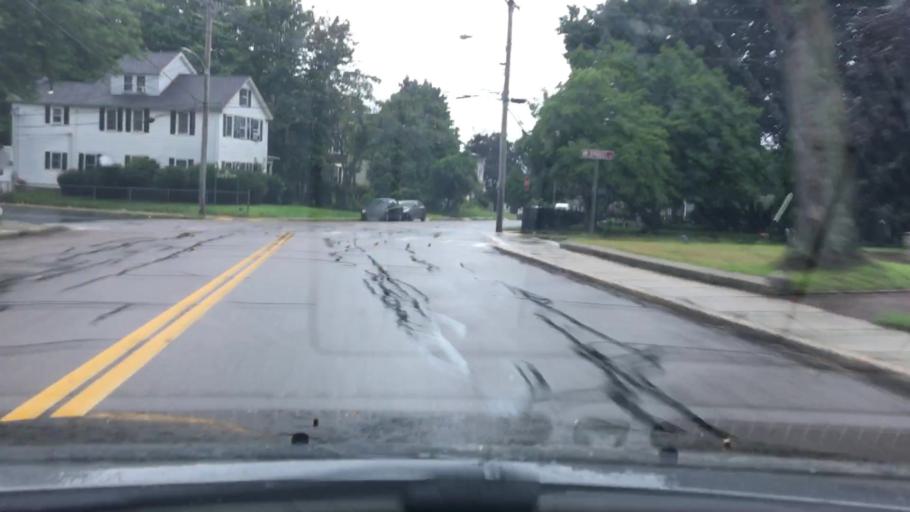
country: US
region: Massachusetts
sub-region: Worcester County
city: Milford
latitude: 42.1438
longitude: -71.5231
